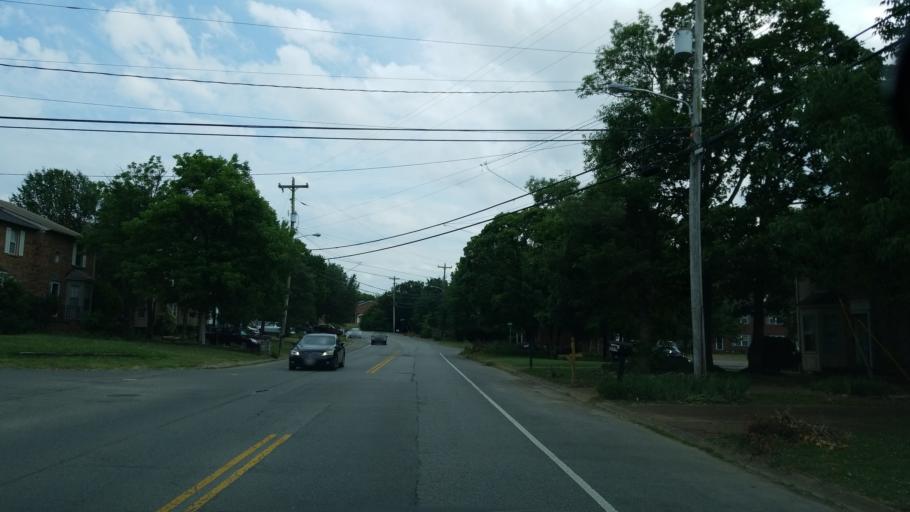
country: US
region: Tennessee
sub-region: Rutherford County
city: La Vergne
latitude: 36.0835
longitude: -86.6125
